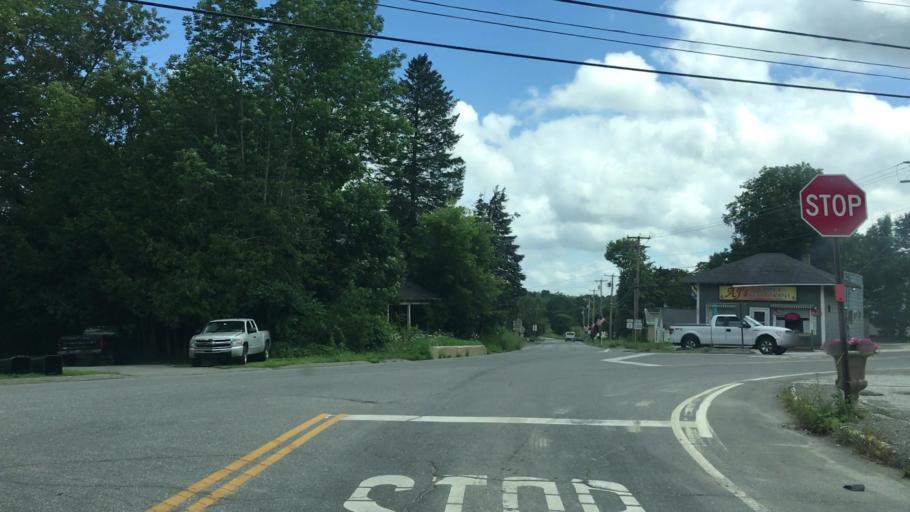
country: US
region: Maine
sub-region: Penobscot County
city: Carmel
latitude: 44.7970
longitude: -69.0512
